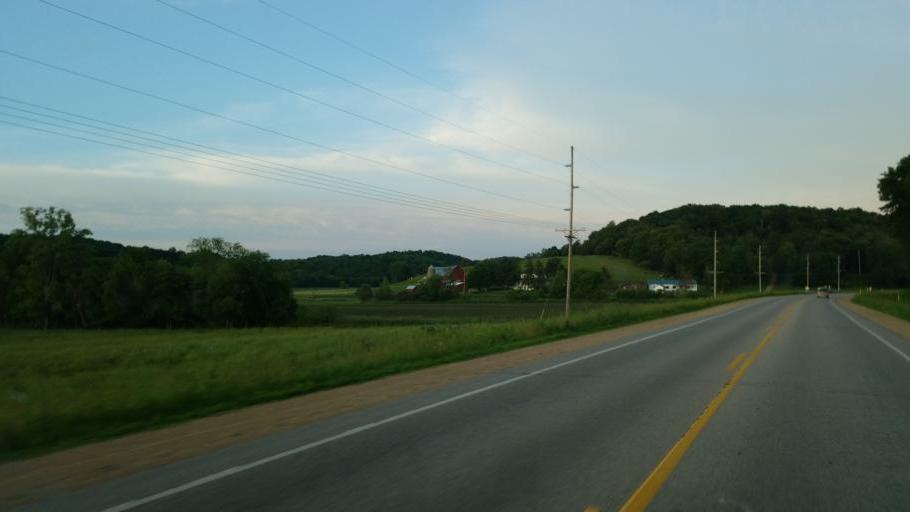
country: US
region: Wisconsin
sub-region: Monroe County
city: Tomah
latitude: 43.8243
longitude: -90.4474
